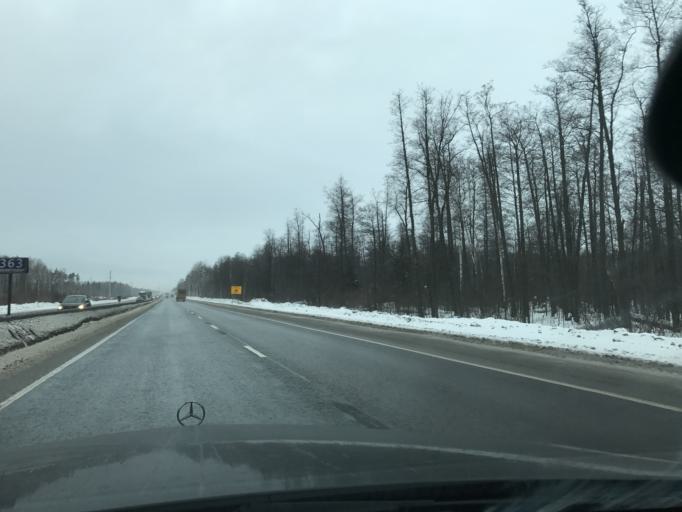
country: RU
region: Nizjnij Novgorod
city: Smolino
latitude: 56.2828
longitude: 43.1170
